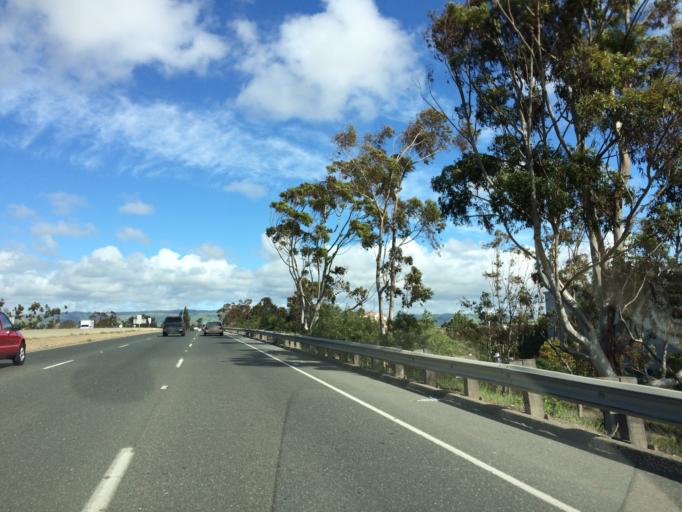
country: US
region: California
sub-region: Alameda County
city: Newark
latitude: 37.5469
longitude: -122.0586
